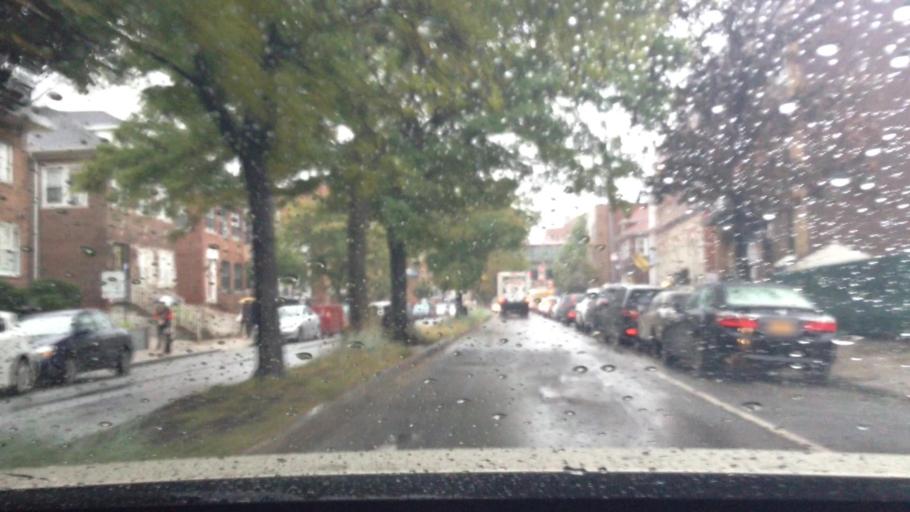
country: US
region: New York
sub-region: Queens County
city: Long Island City
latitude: 40.7486
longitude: -73.8908
